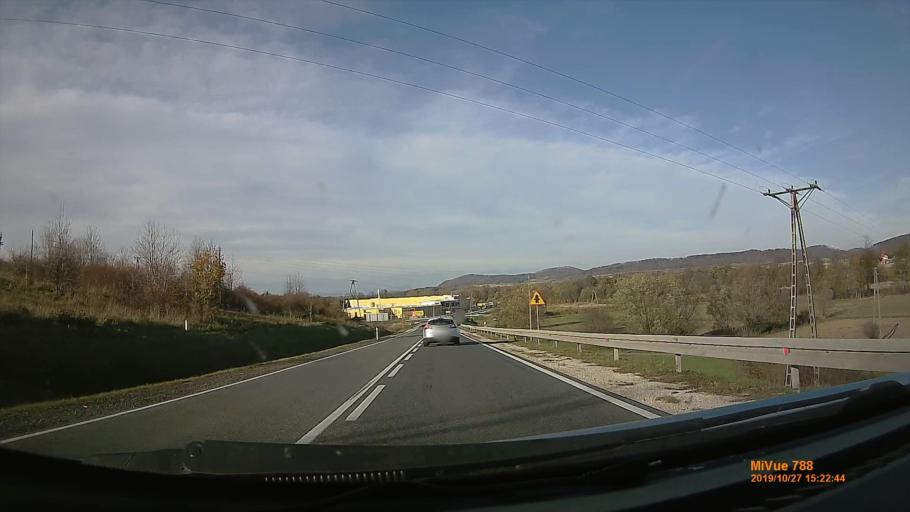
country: PL
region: Lower Silesian Voivodeship
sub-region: Powiat klodzki
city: Bystrzyca Klodzka
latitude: 50.3038
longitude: 16.6607
